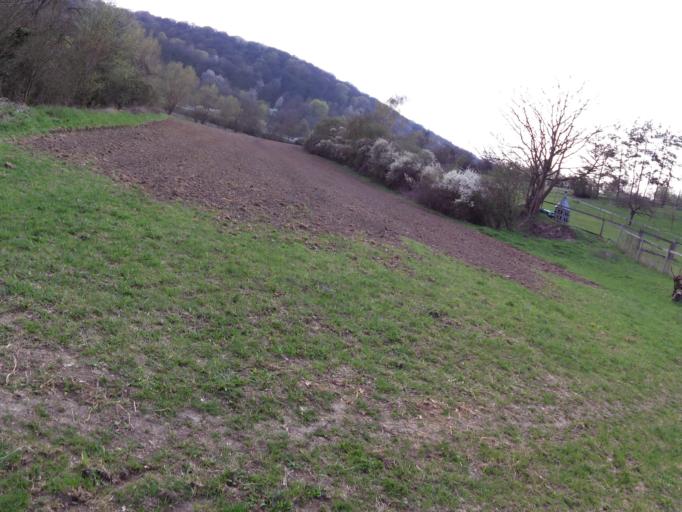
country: DE
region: Bavaria
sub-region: Regierungsbezirk Unterfranken
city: Rottendorf
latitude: 49.7857
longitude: 10.0189
